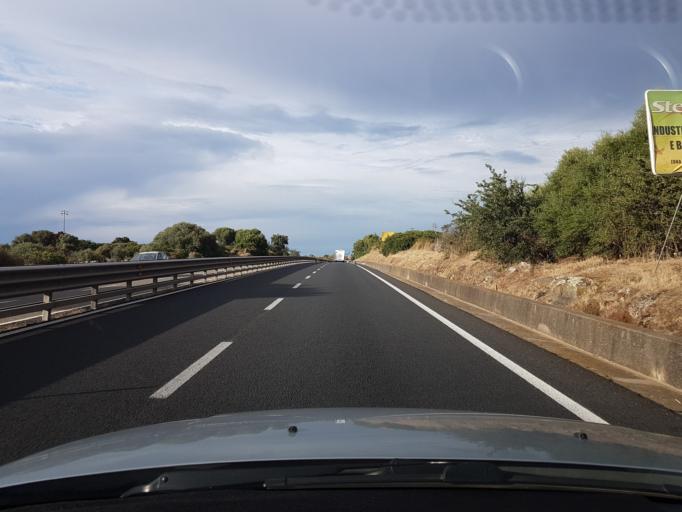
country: IT
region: Sardinia
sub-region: Provincia di Oristano
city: Paulilatino
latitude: 40.0862
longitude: 8.7540
